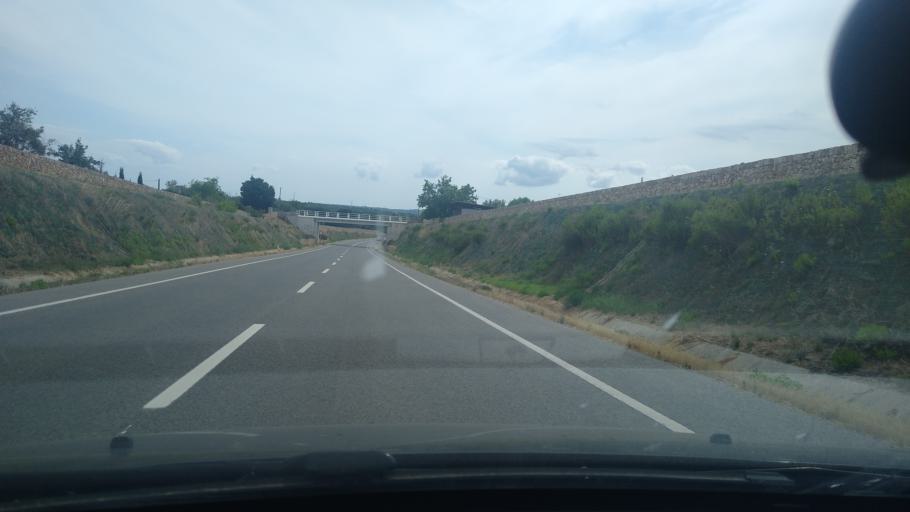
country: ES
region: Balearic Islands
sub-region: Illes Balears
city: Llubi
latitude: 39.6986
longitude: 3.0135
